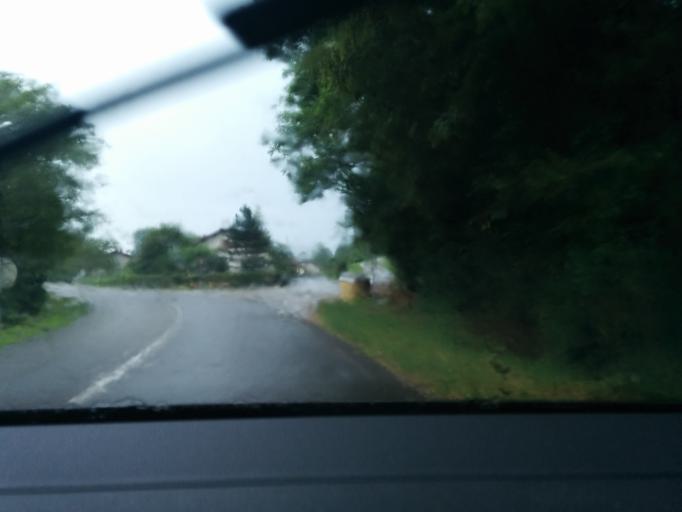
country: FR
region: Franche-Comte
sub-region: Departement du Jura
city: Saint-Lupicin
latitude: 46.4124
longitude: 5.7951
